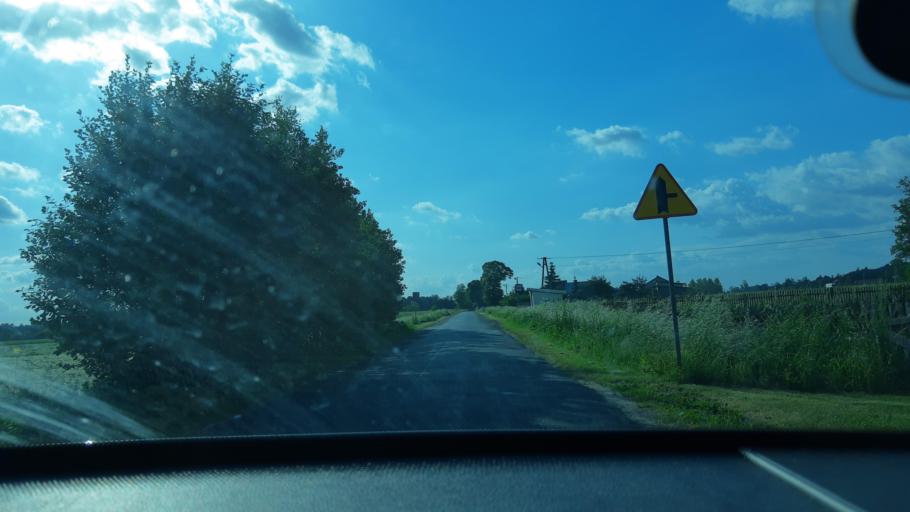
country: PL
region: Lodz Voivodeship
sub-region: Powiat zdunskowolski
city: Zapolice
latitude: 51.5360
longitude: 18.8316
